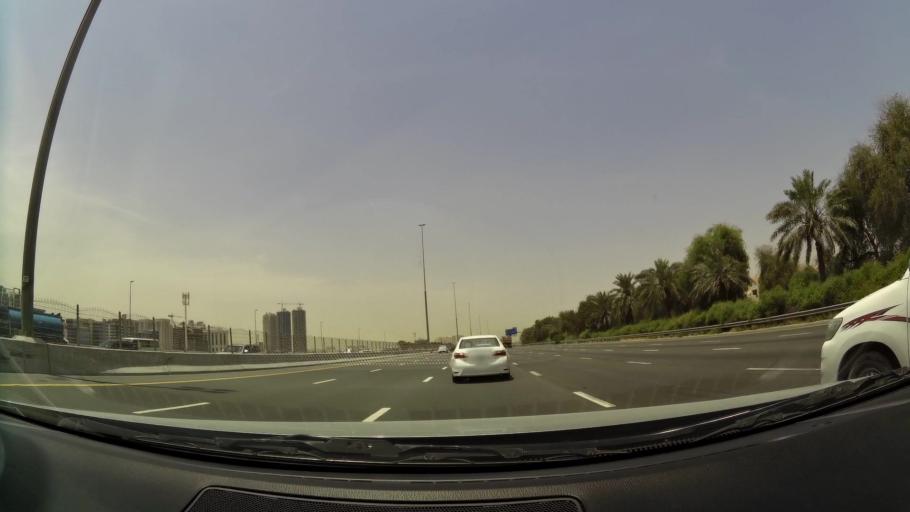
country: AE
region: Dubai
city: Dubai
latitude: 25.1267
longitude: 55.3734
